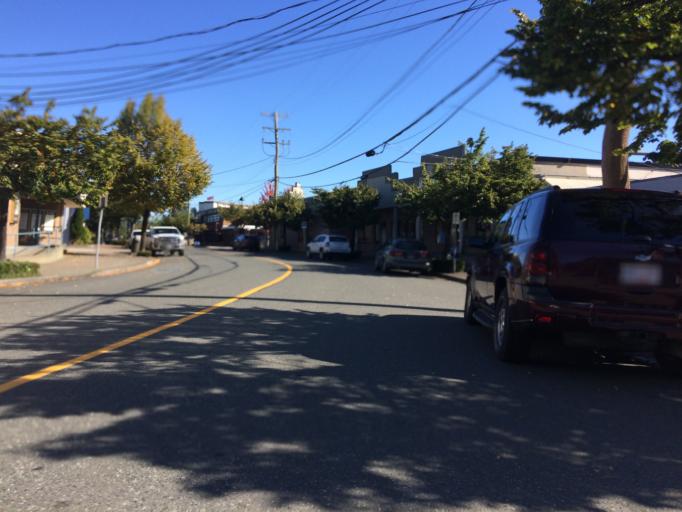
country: CA
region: British Columbia
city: Campbell River
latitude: 50.0251
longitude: -125.2459
